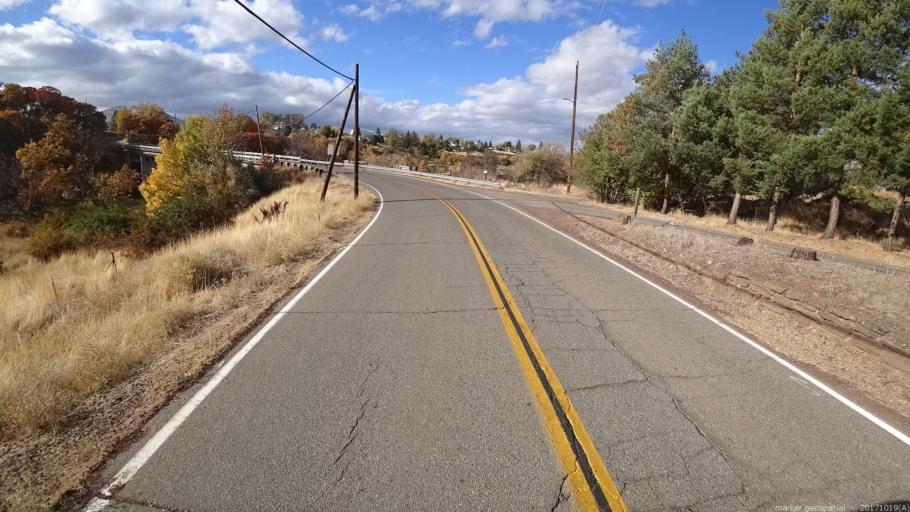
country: US
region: California
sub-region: Shasta County
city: Burney
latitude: 41.0006
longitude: -121.4352
